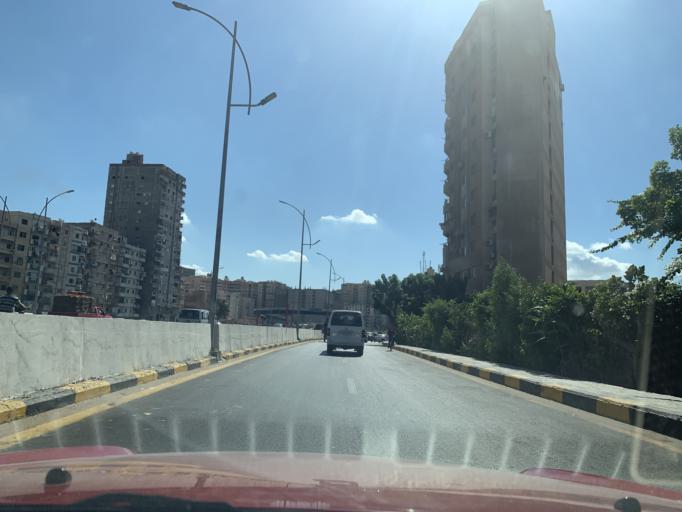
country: EG
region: Alexandria
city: Alexandria
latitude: 31.2150
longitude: 29.9622
